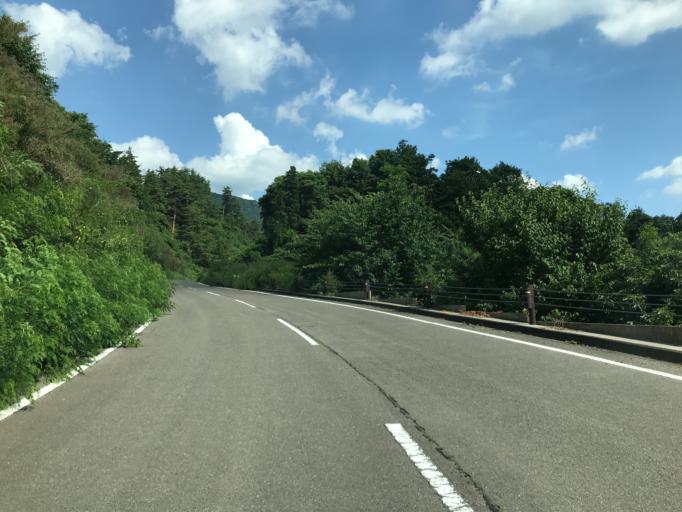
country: JP
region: Fukushima
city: Yanagawamachi-saiwaicho
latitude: 37.7792
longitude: 140.6673
